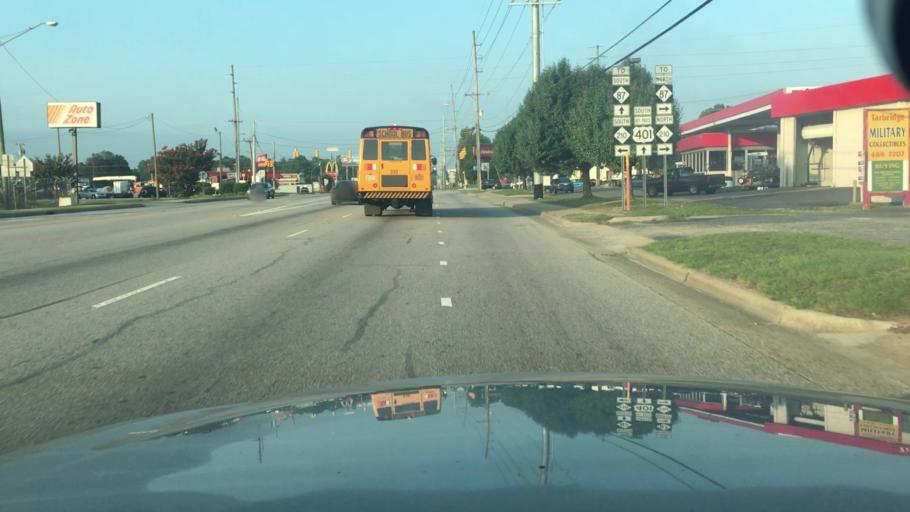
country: US
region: North Carolina
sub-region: Cumberland County
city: Fayetteville
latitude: 35.0983
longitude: -78.9149
